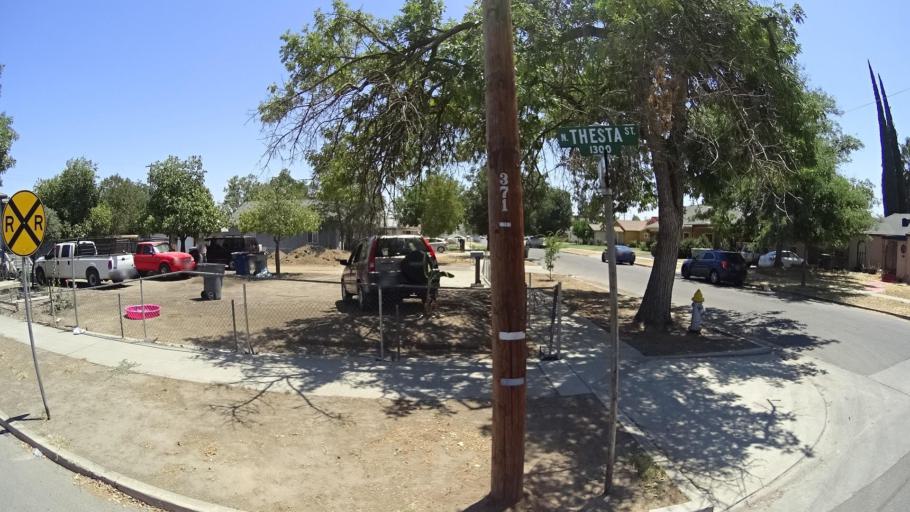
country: US
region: California
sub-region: Fresno County
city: Fresno
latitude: 36.7605
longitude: -119.7838
